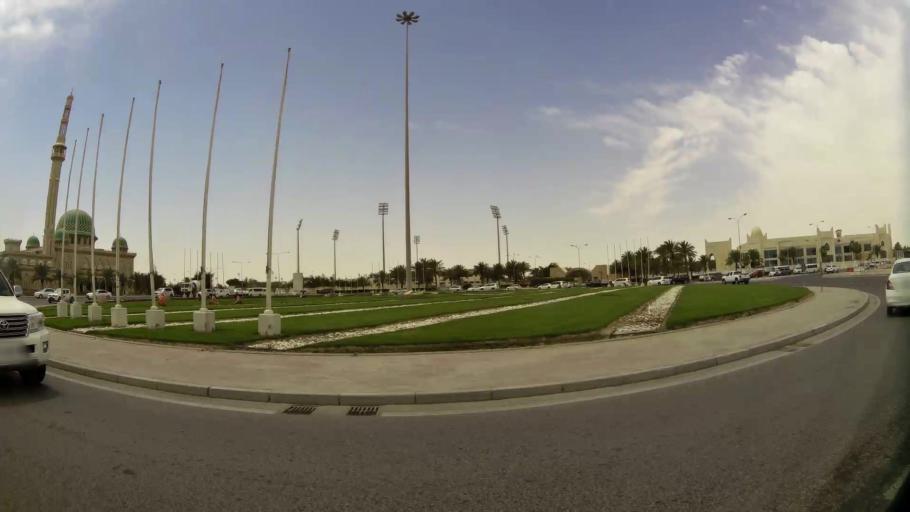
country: QA
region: Baladiyat ar Rayyan
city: Ar Rayyan
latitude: 25.2833
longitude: 51.4327
